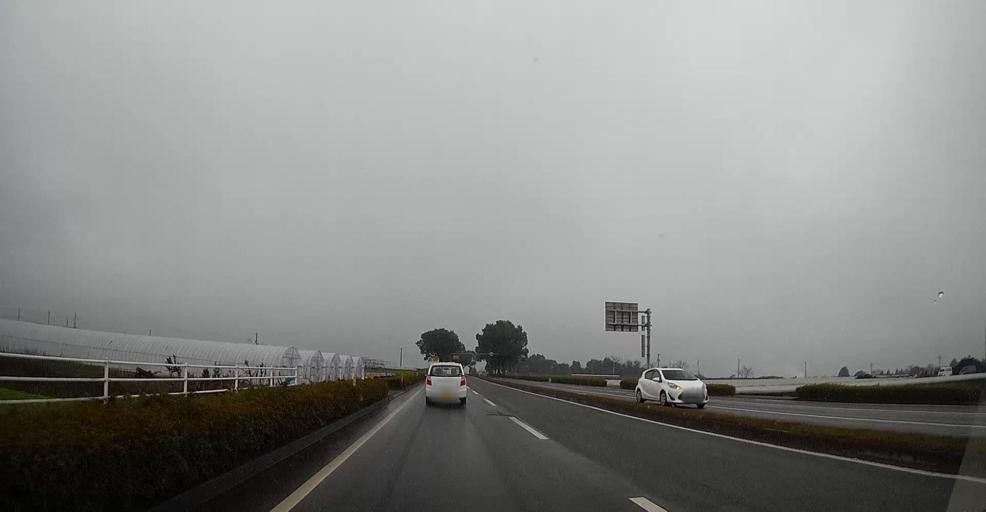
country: JP
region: Kumamoto
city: Ozu
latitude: 32.8285
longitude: 130.8584
